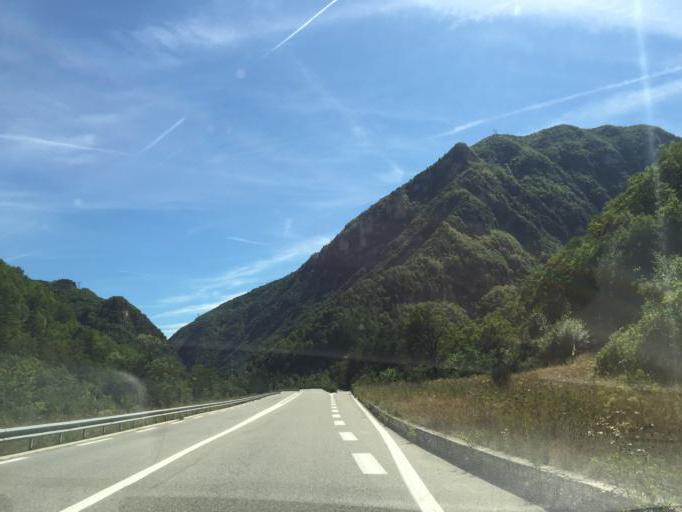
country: FR
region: Provence-Alpes-Cote d'Azur
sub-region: Departement des Alpes-Maritimes
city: Saint-Martin-Vesubie
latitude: 44.0249
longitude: 7.1317
